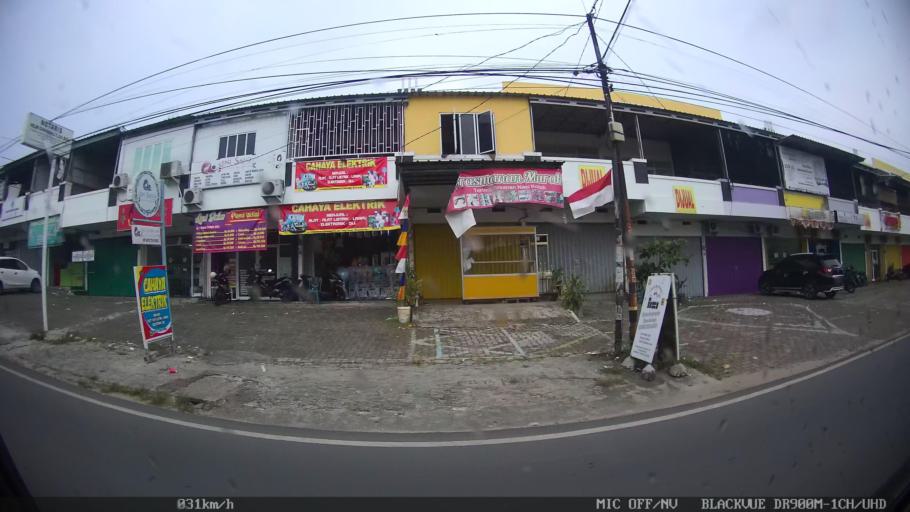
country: ID
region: Lampung
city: Kedaton
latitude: -5.3945
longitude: 105.2779
